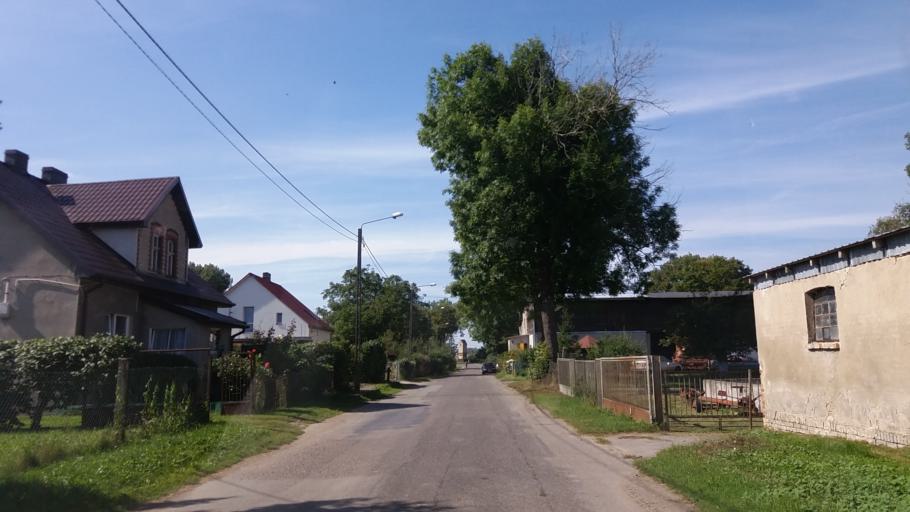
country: PL
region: West Pomeranian Voivodeship
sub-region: Powiat choszczenski
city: Choszczno
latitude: 53.1288
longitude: 15.4101
